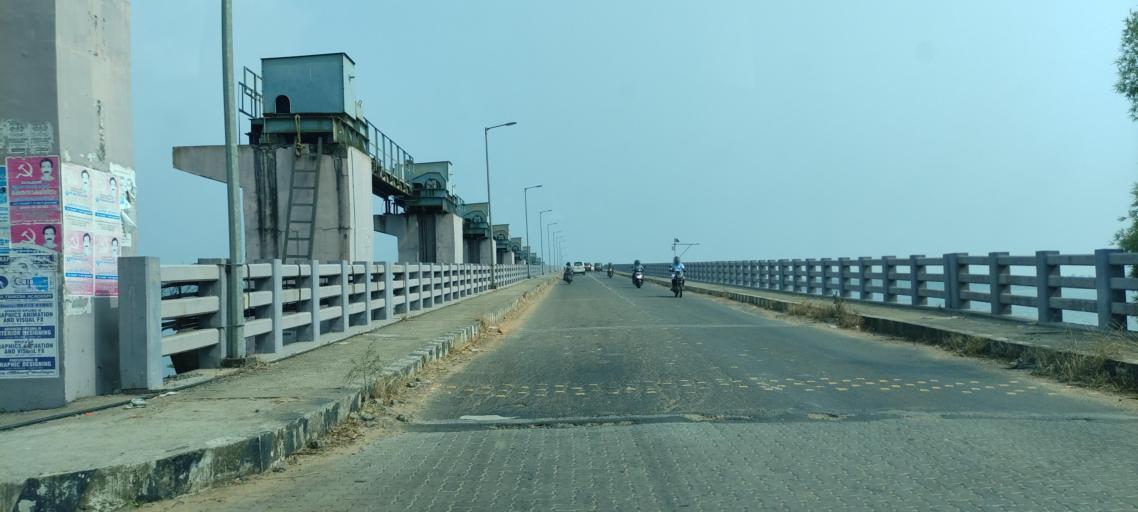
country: IN
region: Kerala
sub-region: Alappuzha
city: Shertallai
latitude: 9.6749
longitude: 76.3980
